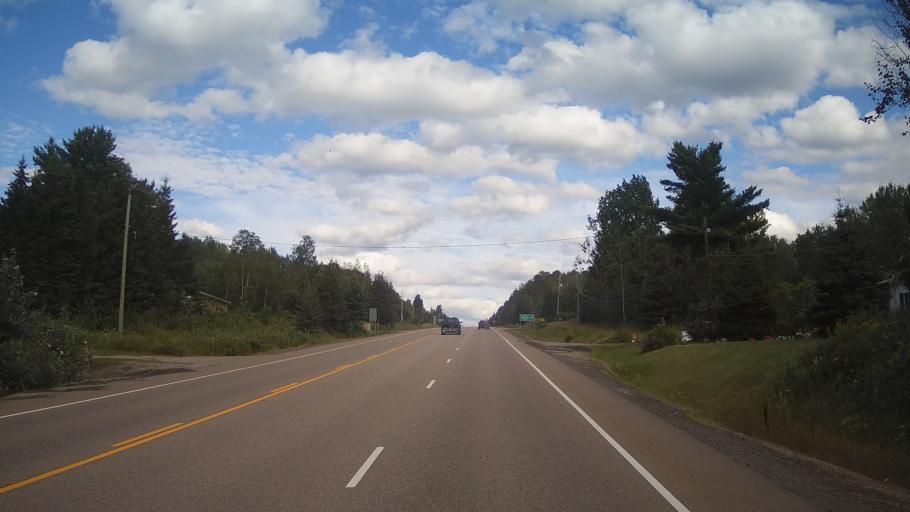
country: CA
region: Ontario
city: Mattawa
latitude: 46.3103
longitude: -78.6623
